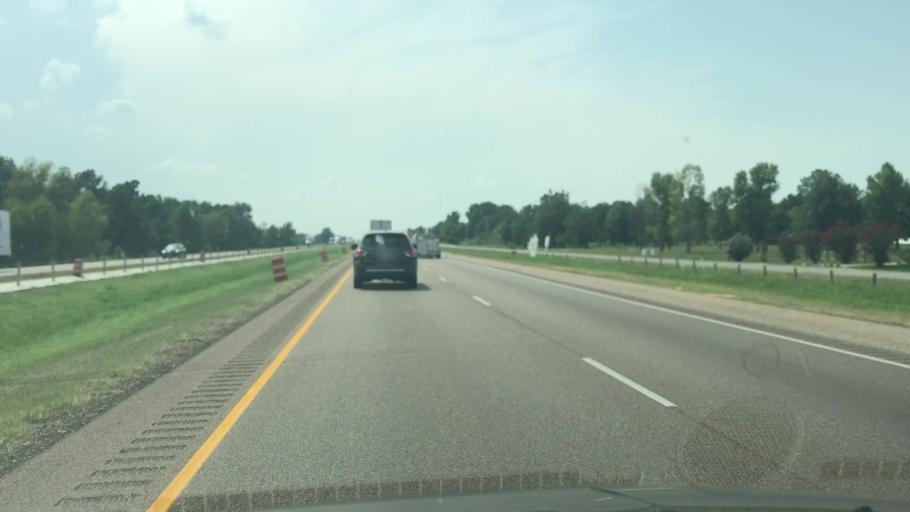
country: US
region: Arkansas
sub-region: Crittenden County
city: Earle
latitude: 35.1501
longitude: -90.3678
